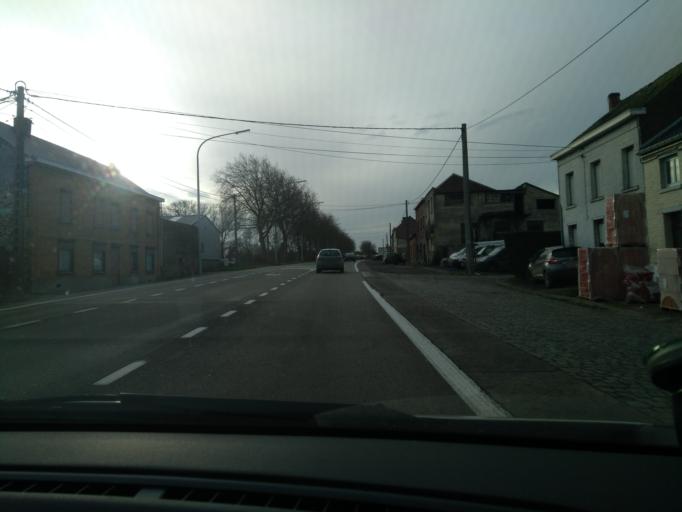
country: BE
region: Wallonia
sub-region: Province du Hainaut
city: Quevy-le-Petit
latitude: 50.3550
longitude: 3.9675
